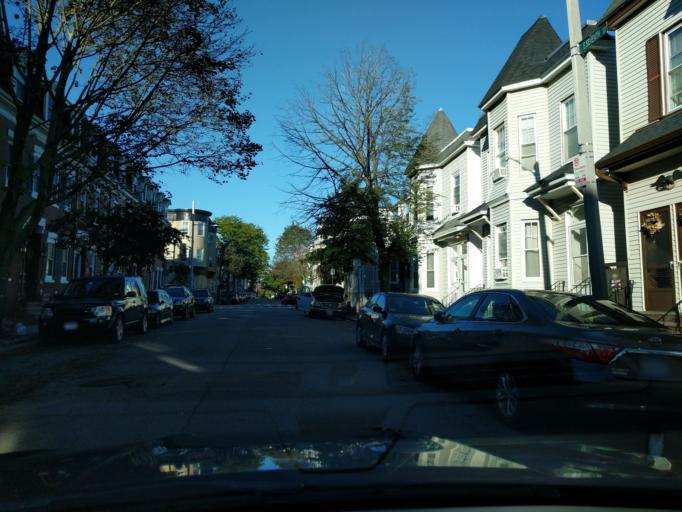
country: US
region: Massachusetts
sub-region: Suffolk County
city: South Boston
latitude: 42.3323
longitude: -71.0326
